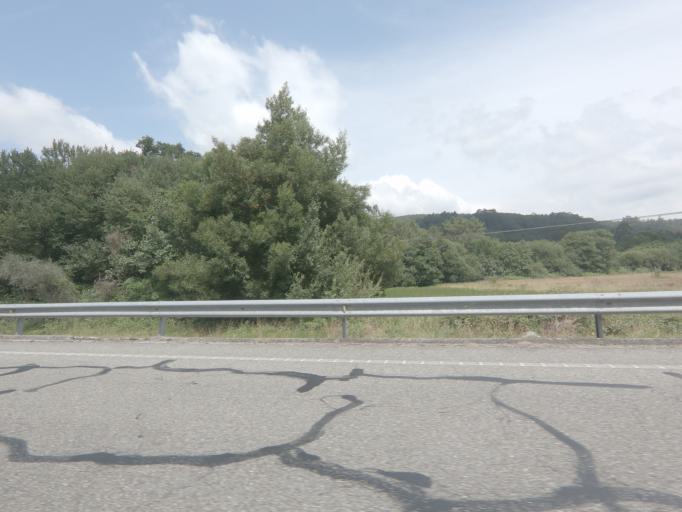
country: ES
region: Galicia
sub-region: Provincia de Pontevedra
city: Tomino
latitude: 42.0218
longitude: -8.7327
